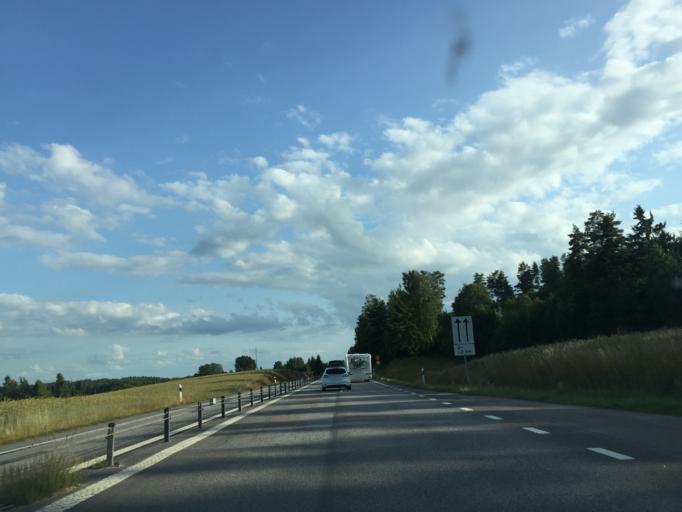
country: SE
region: OEstergoetland
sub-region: Motala Kommun
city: Motala
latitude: 58.5879
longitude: 14.9878
